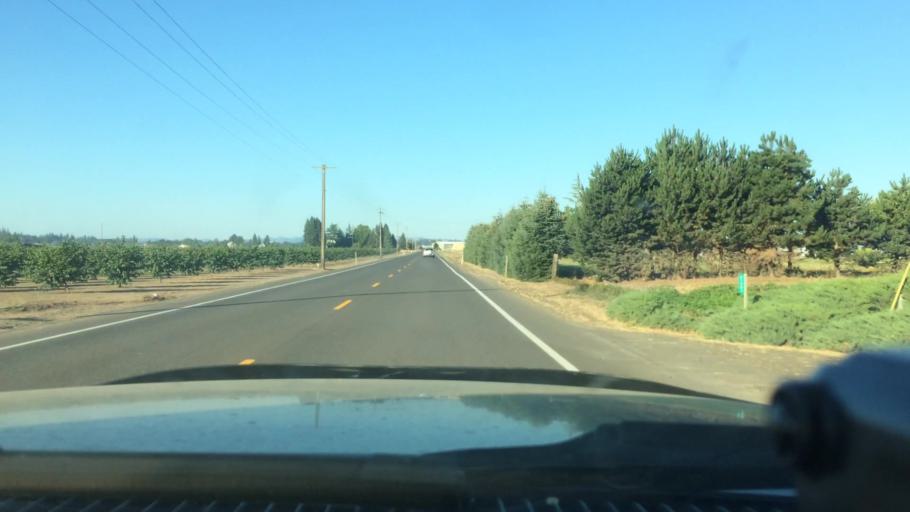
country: US
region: Oregon
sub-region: Yamhill County
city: Newberg
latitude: 45.2374
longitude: -122.9584
